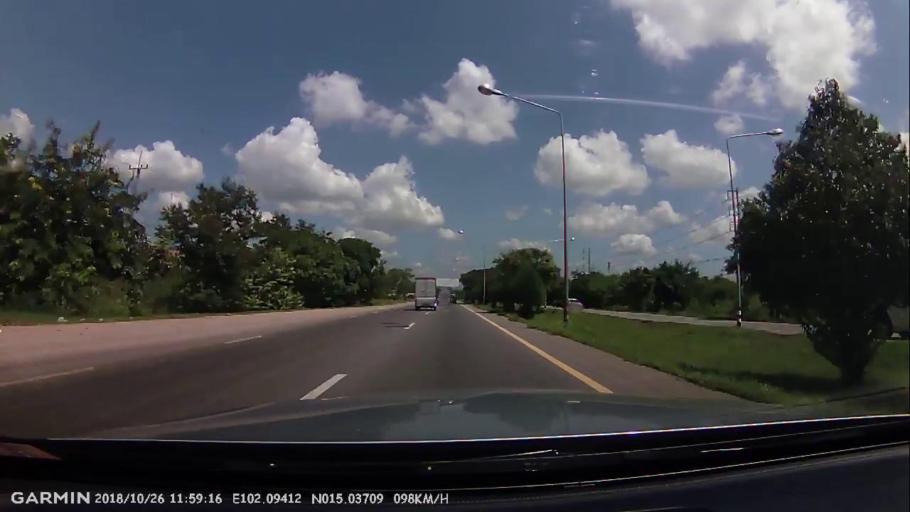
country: TH
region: Nakhon Ratchasima
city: Nakhon Ratchasima
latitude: 15.0372
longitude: 102.0943
